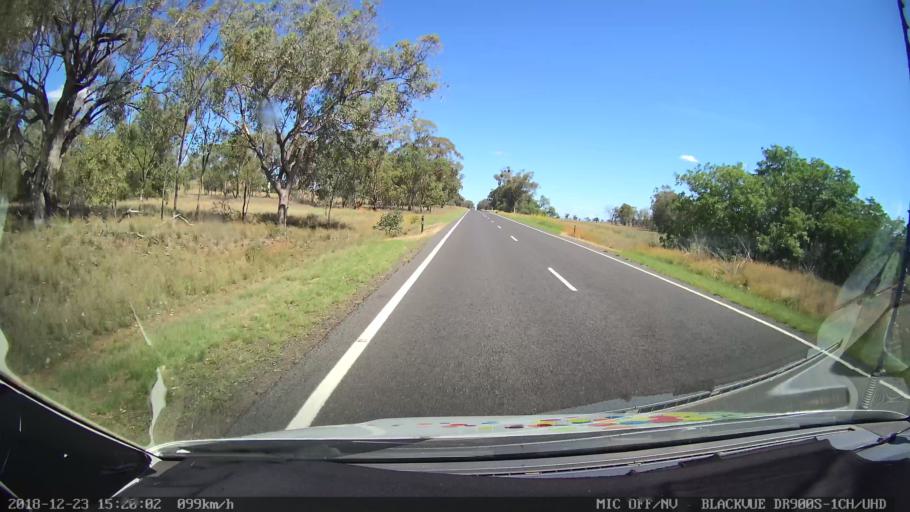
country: AU
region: New South Wales
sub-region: Tamworth Municipality
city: Manilla
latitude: -30.8372
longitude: 150.7870
